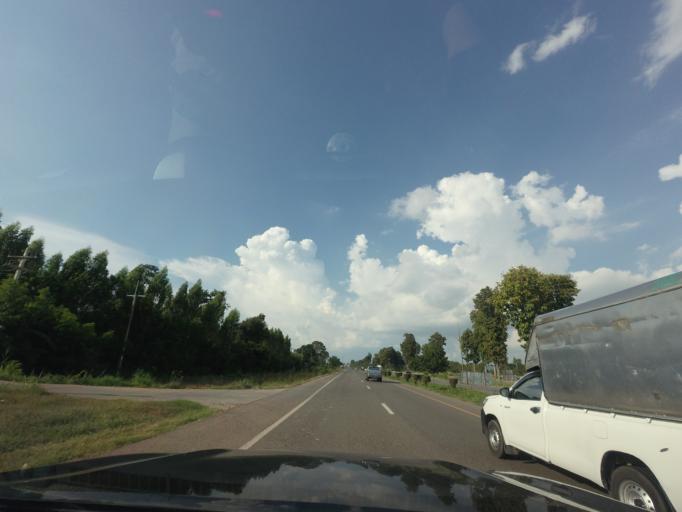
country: TH
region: Khon Kaen
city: Ban Haet
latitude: 16.1496
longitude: 102.7513
